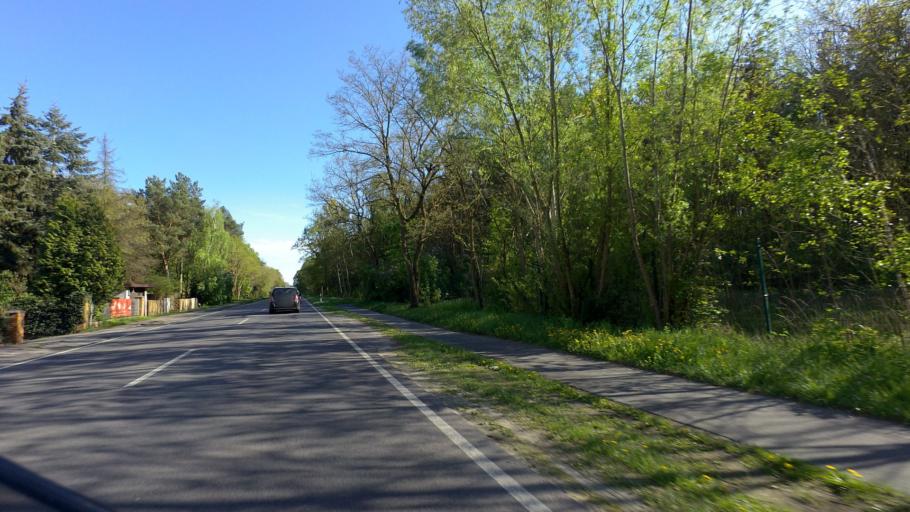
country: DE
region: Brandenburg
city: Oranienburg
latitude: 52.7212
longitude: 13.2518
